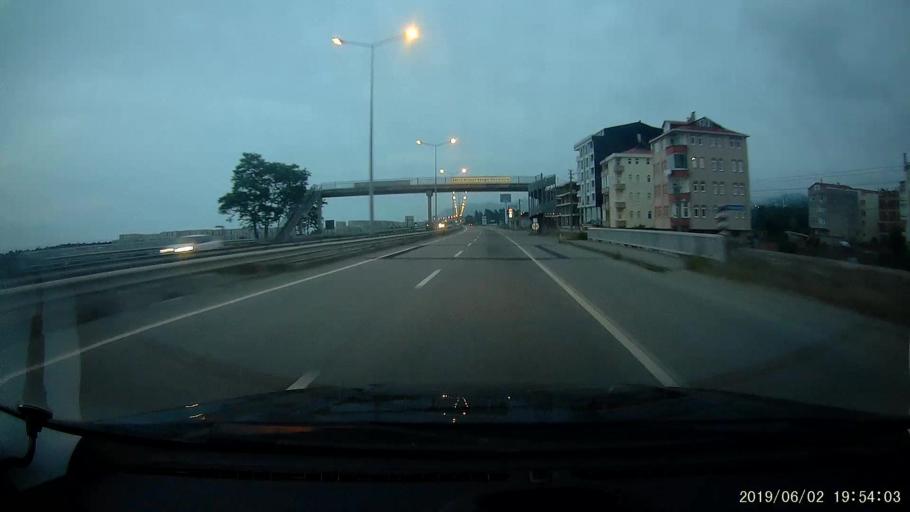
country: TR
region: Trabzon
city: Espiye
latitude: 40.9523
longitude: 38.7199
